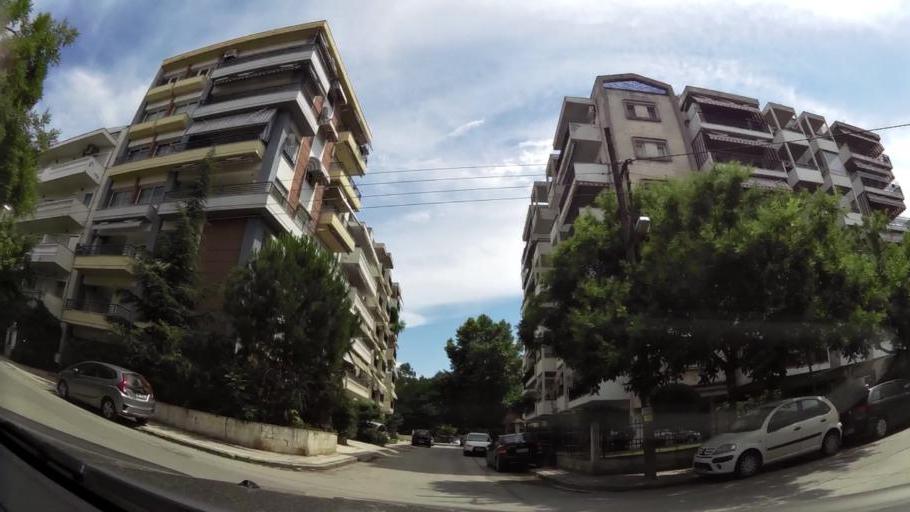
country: GR
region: Central Macedonia
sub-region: Nomos Thessalonikis
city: Pylaia
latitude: 40.6042
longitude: 22.9793
